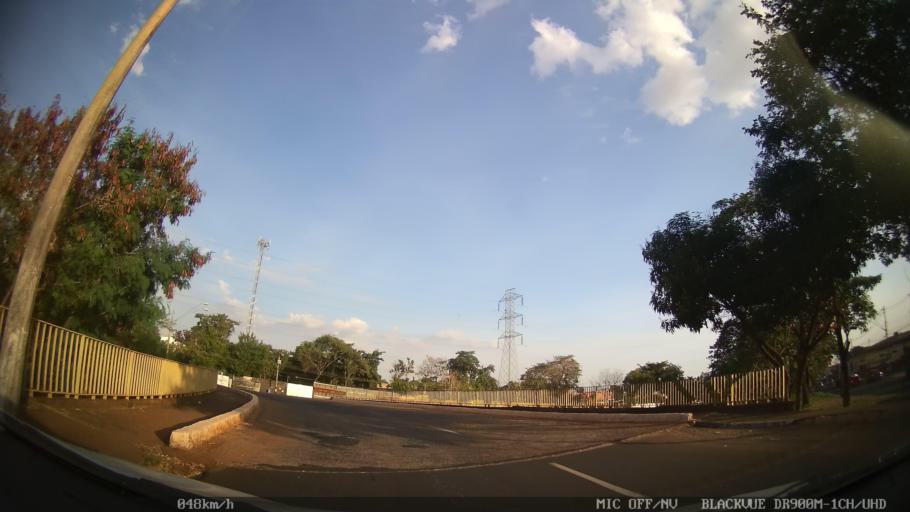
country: BR
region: Sao Paulo
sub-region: Ribeirao Preto
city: Ribeirao Preto
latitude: -21.1454
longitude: -47.8044
